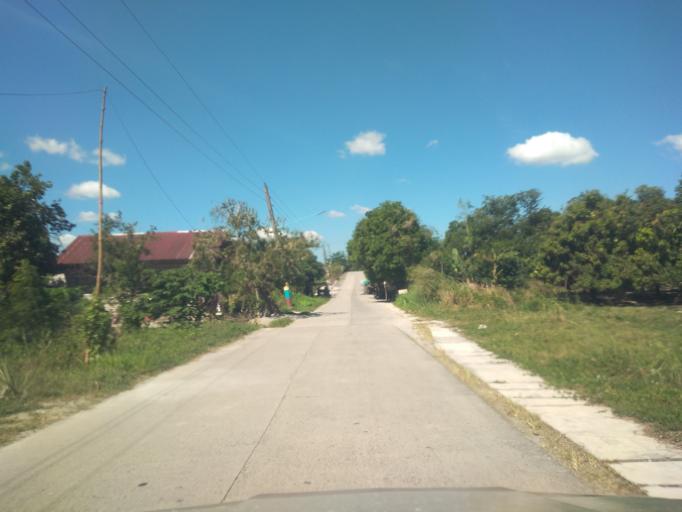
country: PH
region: Central Luzon
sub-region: Province of Pampanga
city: Magliman
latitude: 15.0292
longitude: 120.6308
